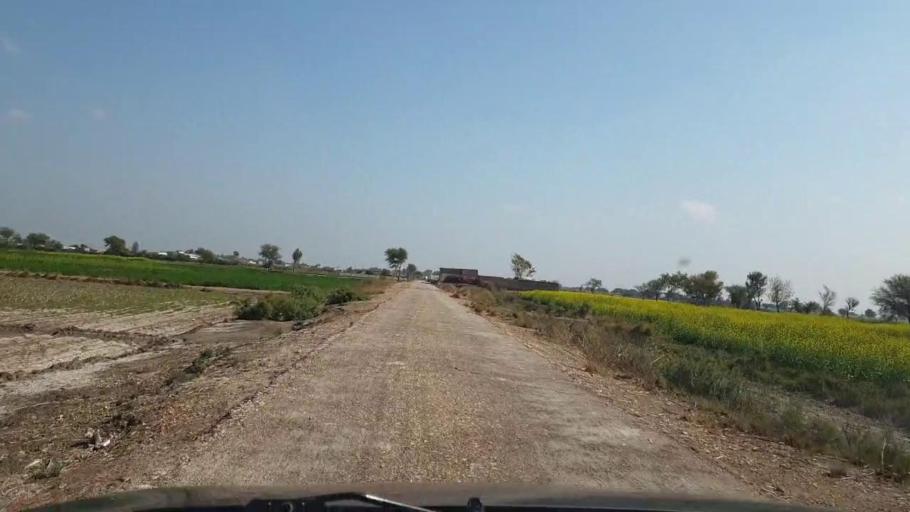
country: PK
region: Sindh
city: Sinjhoro
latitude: 26.0598
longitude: 68.7503
